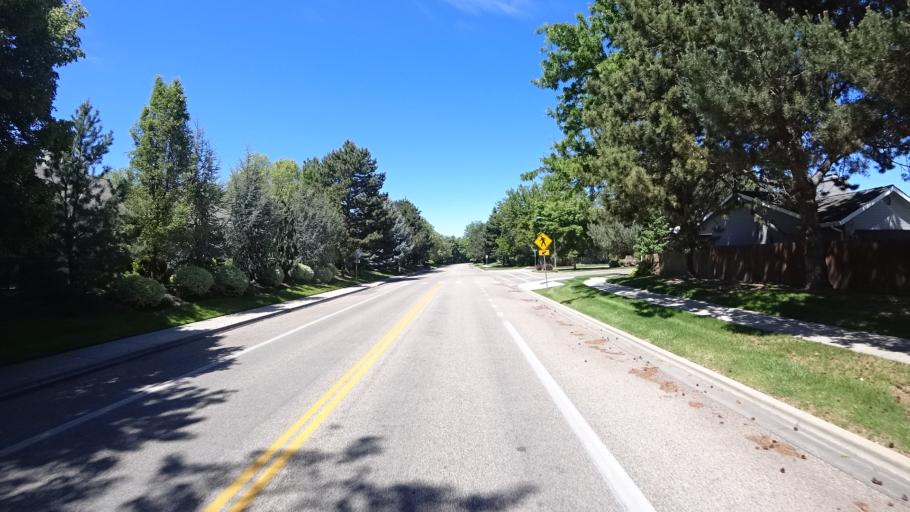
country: US
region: Idaho
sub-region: Ada County
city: Boise
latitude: 43.5693
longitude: -116.1790
